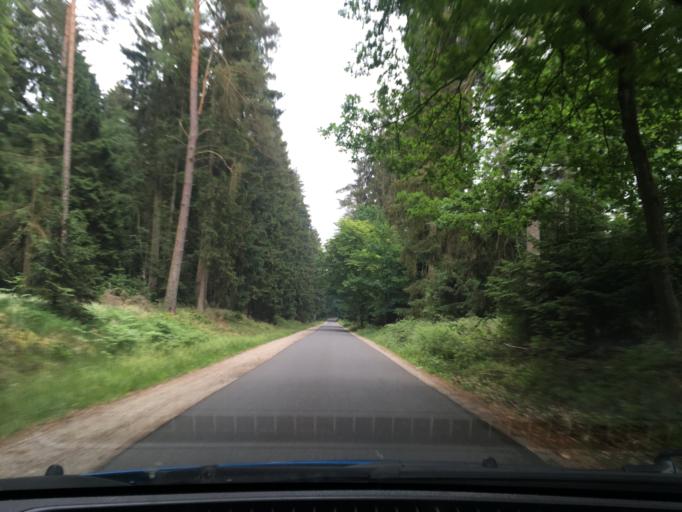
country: DE
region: Lower Saxony
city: Gohrde
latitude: 53.1195
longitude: 10.8600
